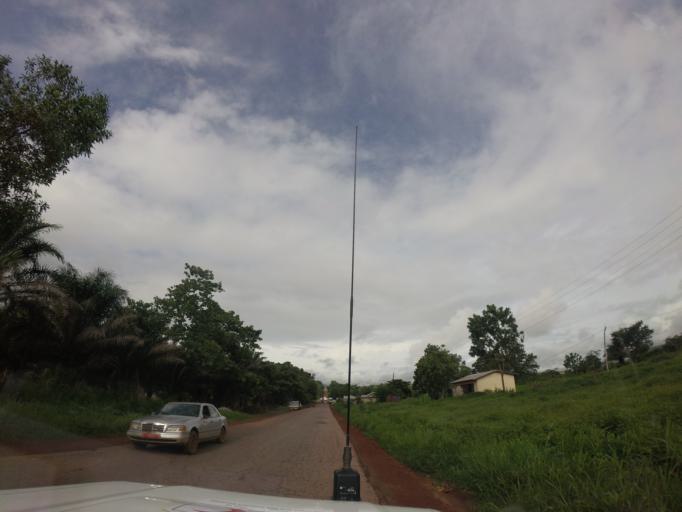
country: GN
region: Kindia
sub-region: Coyah
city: Coyah
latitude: 9.8157
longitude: -13.2660
